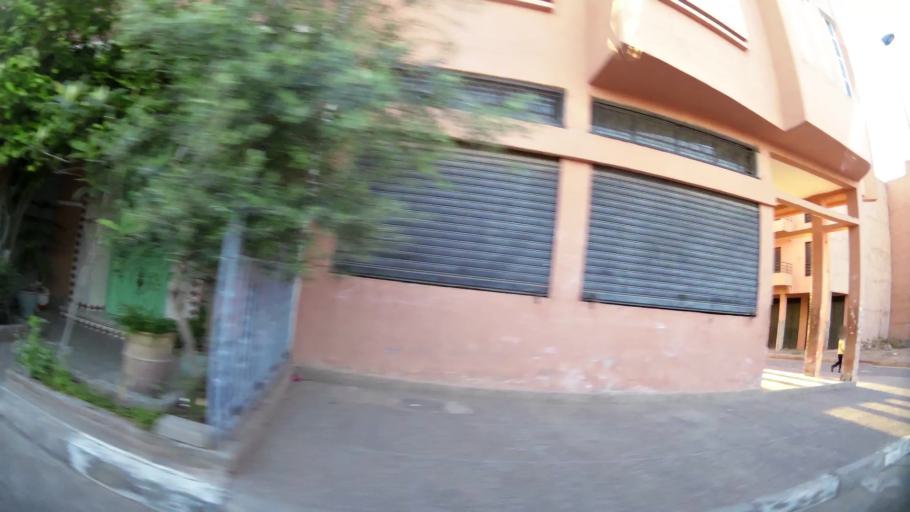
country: MA
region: Marrakech-Tensift-Al Haouz
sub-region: Marrakech
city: Marrakesh
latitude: 31.6421
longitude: -8.0398
